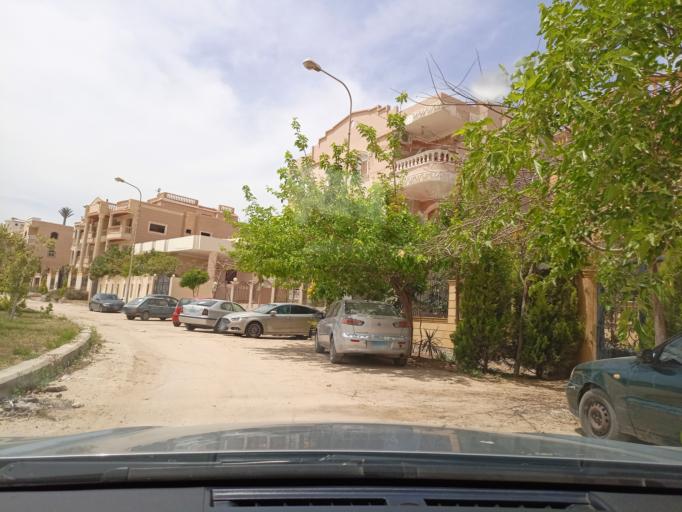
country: EG
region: Muhafazat al Qalyubiyah
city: Al Khankah
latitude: 30.2283
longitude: 31.4880
